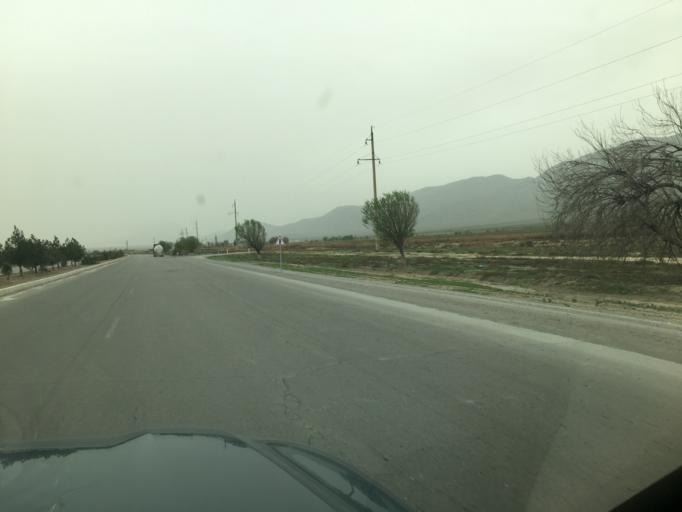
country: TM
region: Ahal
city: Arcabil
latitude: 38.2004
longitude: 57.8262
